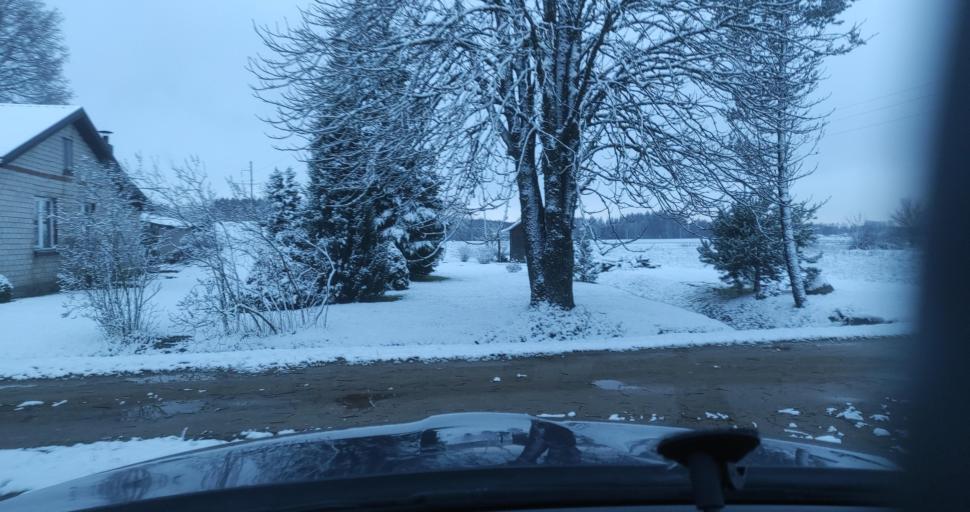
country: LV
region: Skrunda
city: Skrunda
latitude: 56.8704
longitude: 22.2326
